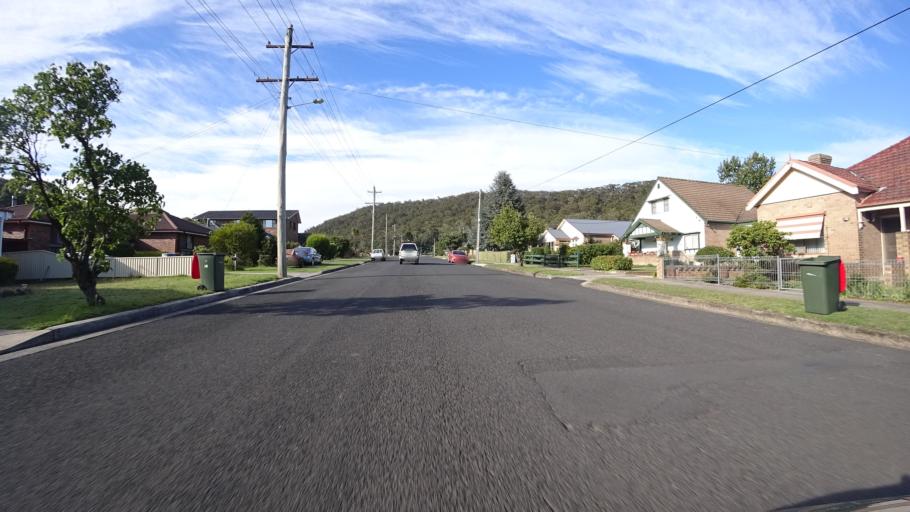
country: AU
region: New South Wales
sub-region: Lithgow
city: Lithgow
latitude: -33.4900
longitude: 150.1509
